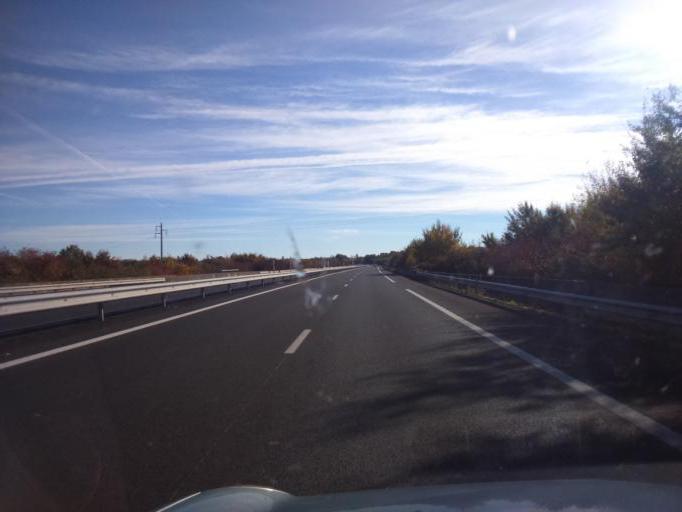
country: FR
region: Poitou-Charentes
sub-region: Departement de la Charente-Maritime
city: Tonnay-Charente
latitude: 45.9564
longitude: -0.9107
